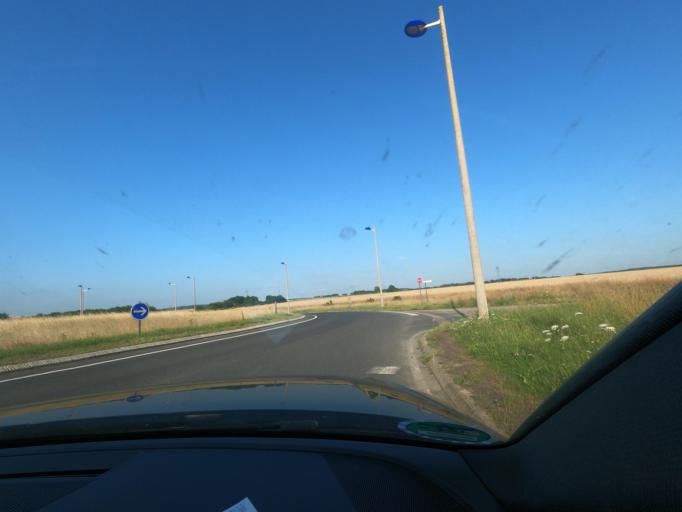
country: FR
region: Picardie
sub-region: Departement de la Somme
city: Pont-de-Metz
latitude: 49.8954
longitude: 2.2462
